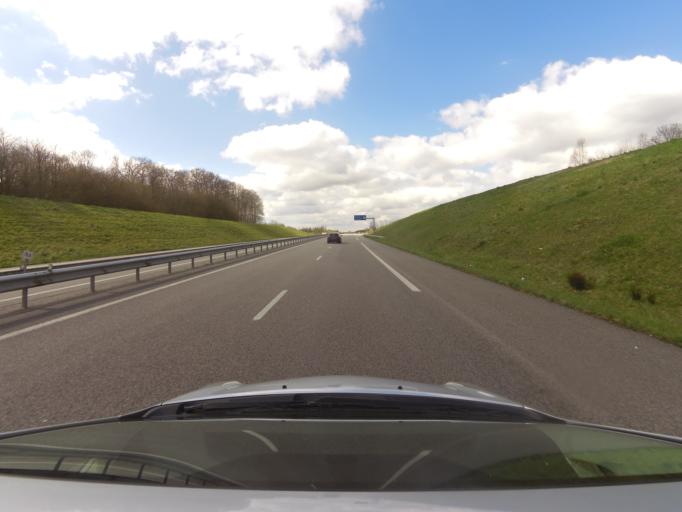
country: FR
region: Haute-Normandie
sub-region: Departement de la Seine-Maritime
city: Yerville
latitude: 49.6563
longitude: 0.8893
